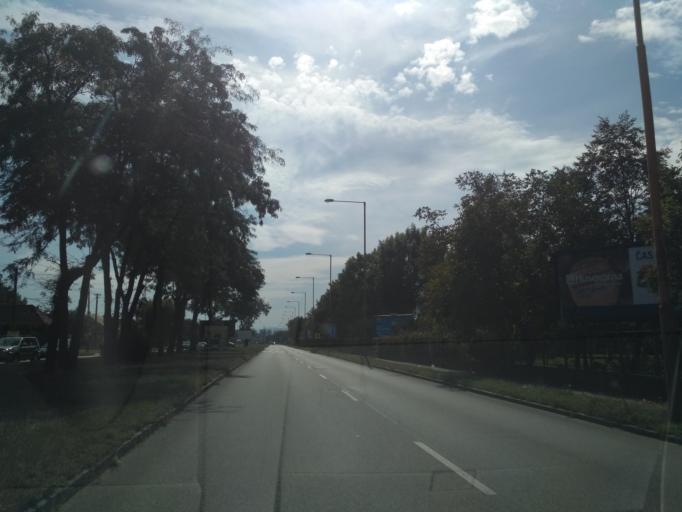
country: SK
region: Kosicky
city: Kosice
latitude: 48.6776
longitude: 21.2691
